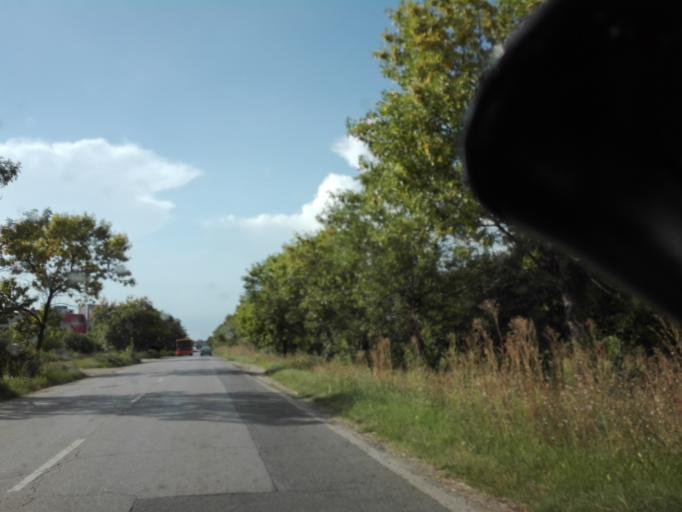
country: BG
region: Sofia-Capital
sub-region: Stolichna Obshtina
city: Sofia
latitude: 42.6239
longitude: 23.4489
